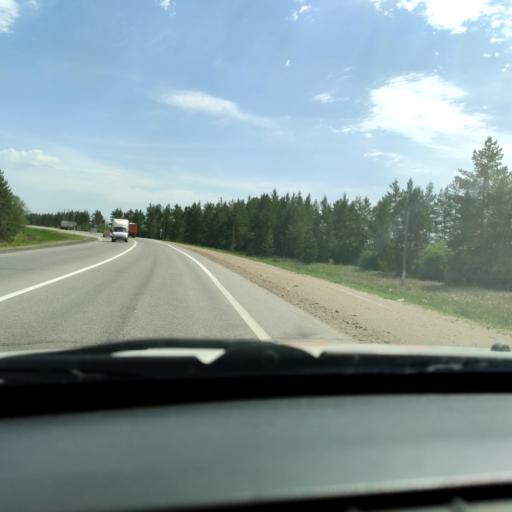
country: RU
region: Samara
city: Mirnyy
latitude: 53.5308
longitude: 50.3050
